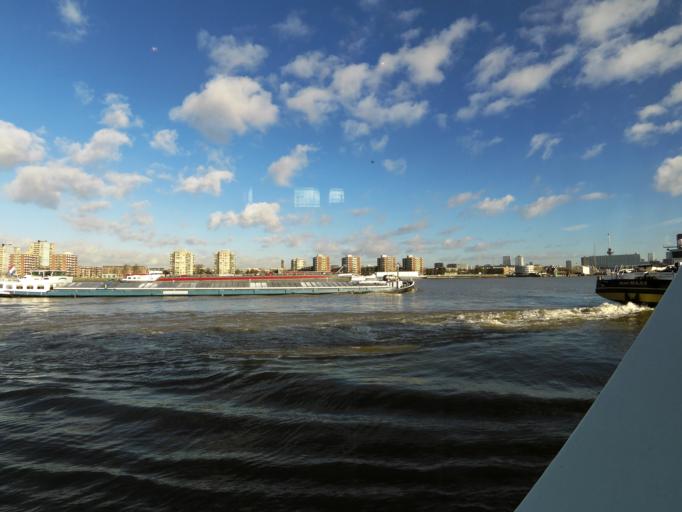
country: NL
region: South Holland
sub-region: Gemeente Rotterdam
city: Delfshaven
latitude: 51.8997
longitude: 4.4416
